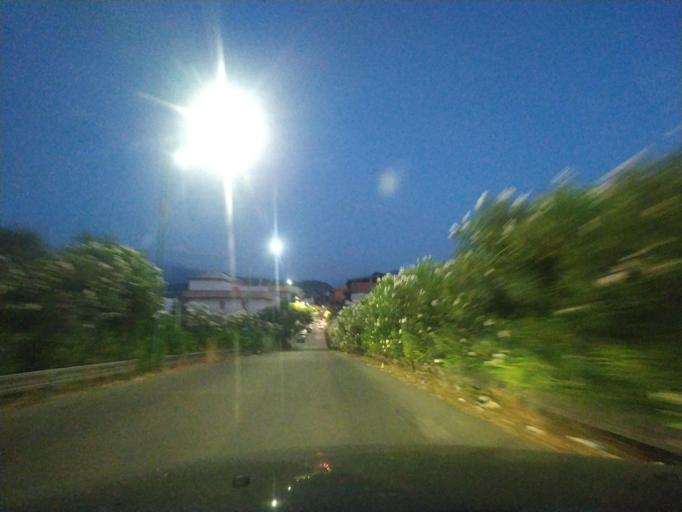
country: IT
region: Sicily
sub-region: Messina
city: Terme
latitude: 38.1409
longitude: 15.1607
